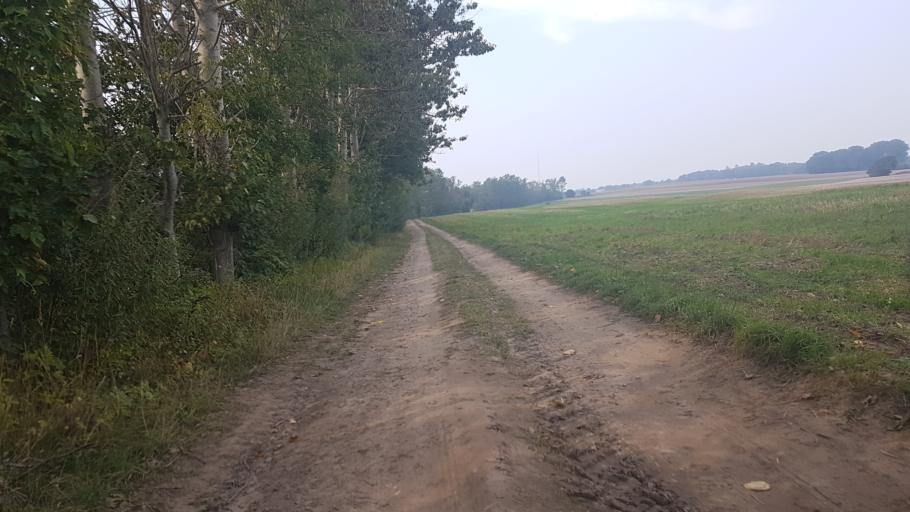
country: DE
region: Mecklenburg-Vorpommern
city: Garz
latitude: 54.2999
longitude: 13.3615
